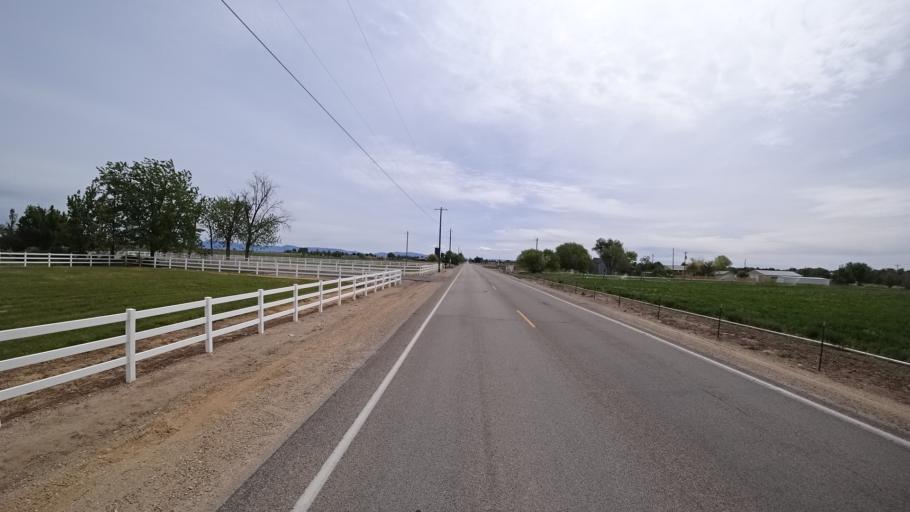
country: US
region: Idaho
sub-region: Ada County
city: Kuna
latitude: 43.5612
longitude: -116.4649
